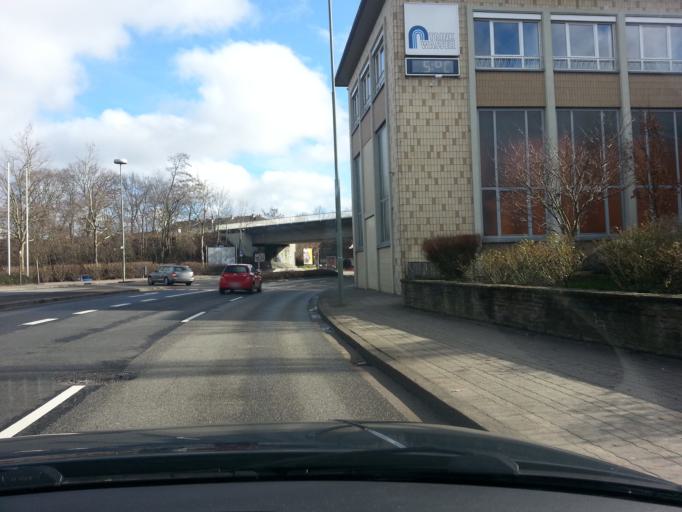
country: DE
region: Rheinland-Pfalz
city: Kaiserslautern
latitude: 49.4412
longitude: 7.7864
